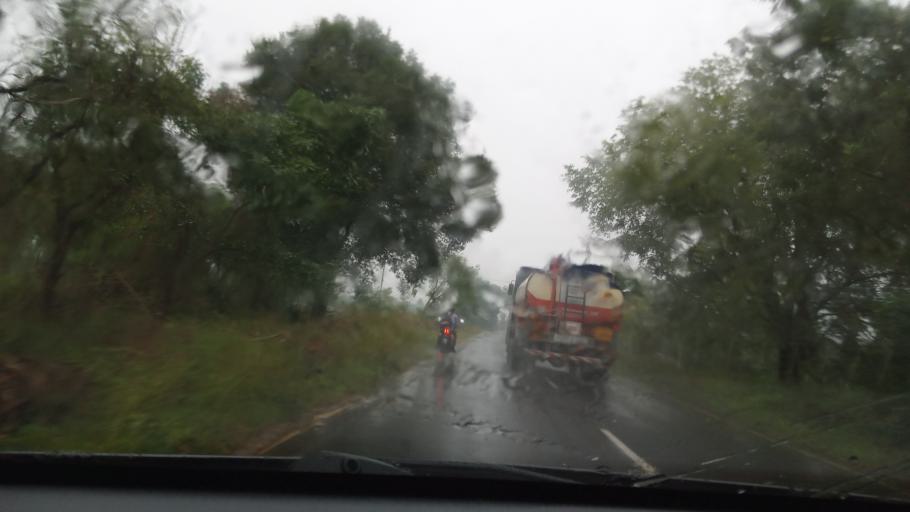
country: IN
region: Tamil Nadu
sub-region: Vellore
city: Kalavai
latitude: 12.8207
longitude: 79.4102
